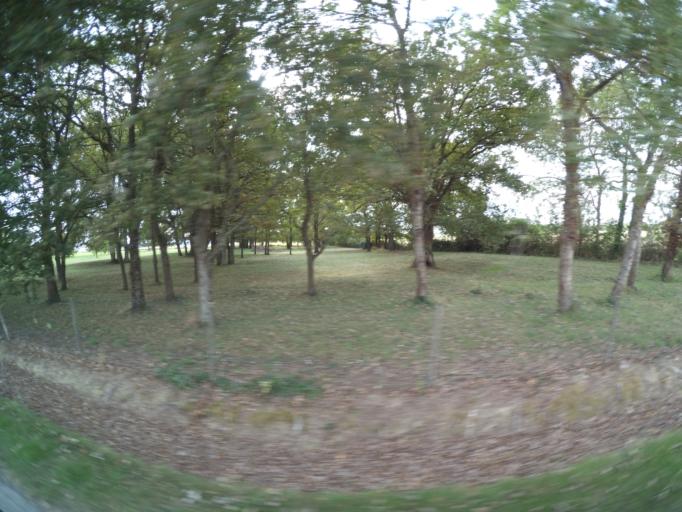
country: FR
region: Centre
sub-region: Departement d'Indre-et-Loire
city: Nazelles-Negron
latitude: 47.4830
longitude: 0.9389
